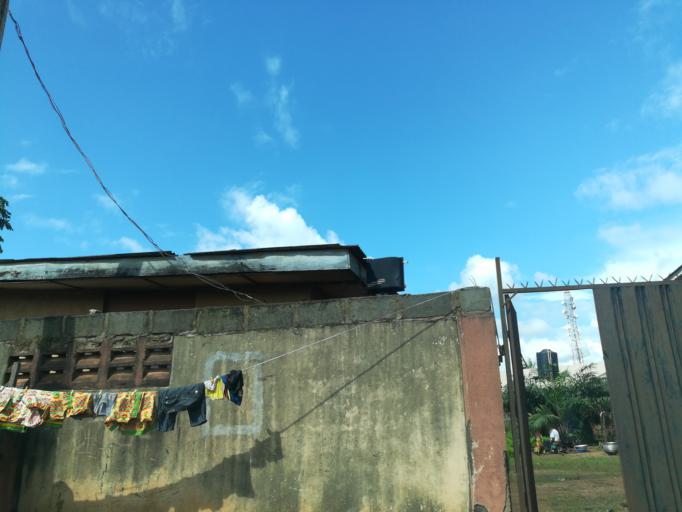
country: NG
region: Lagos
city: Ikorodu
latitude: 6.5935
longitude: 3.5183
